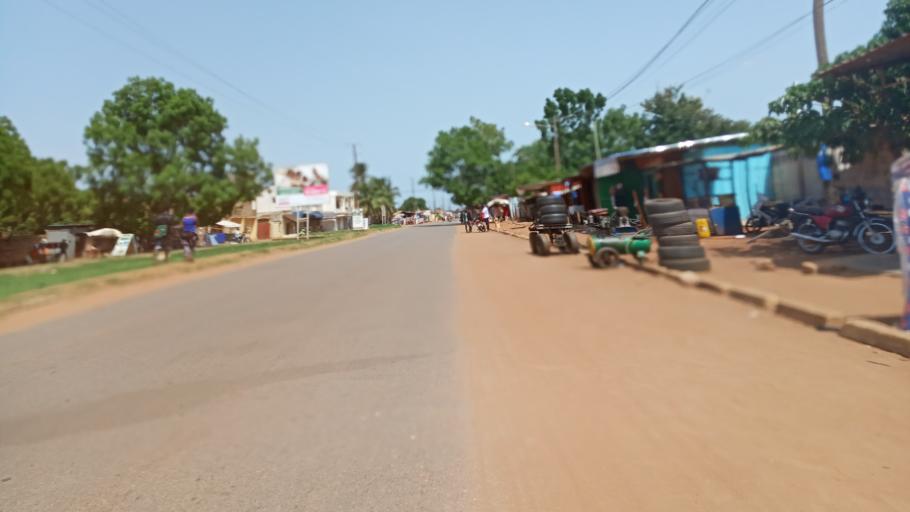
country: TG
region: Maritime
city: Lome
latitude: 6.2262
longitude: 1.2036
